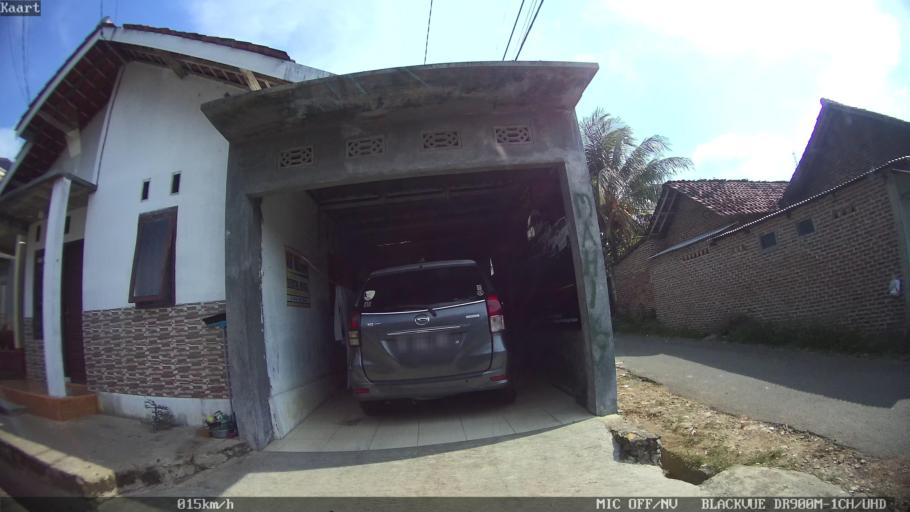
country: ID
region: Lampung
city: Kedaton
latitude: -5.3878
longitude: 105.2308
